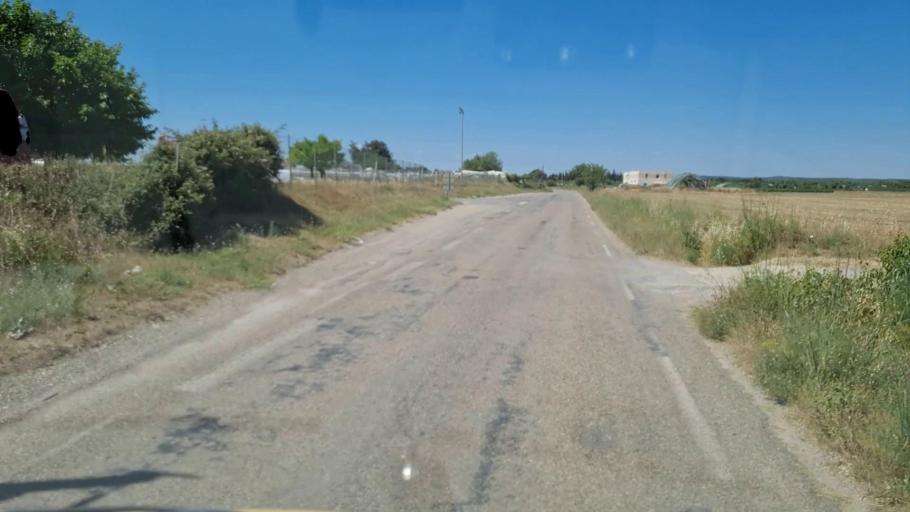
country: FR
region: Languedoc-Roussillon
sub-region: Departement du Gard
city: Codognan
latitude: 43.7173
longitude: 4.2266
